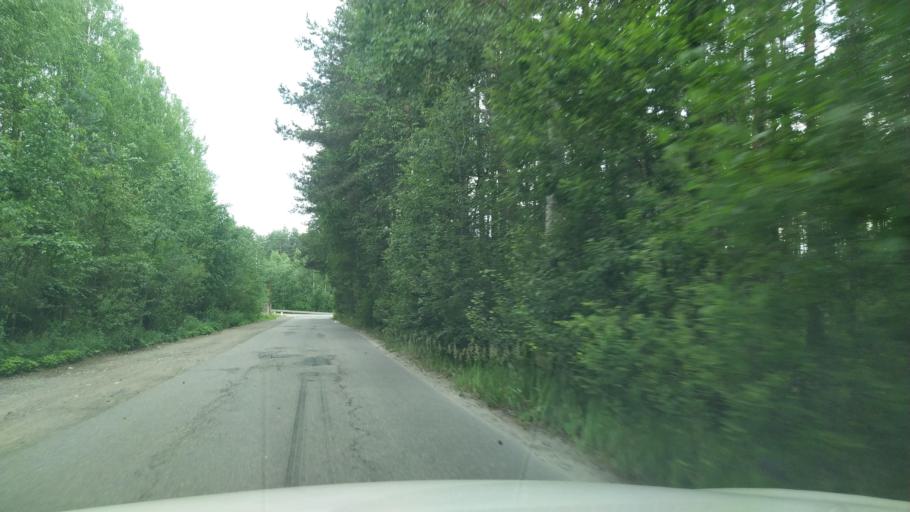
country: RU
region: St.-Petersburg
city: Bol'shaya Izhora
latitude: 59.9170
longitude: 29.5602
